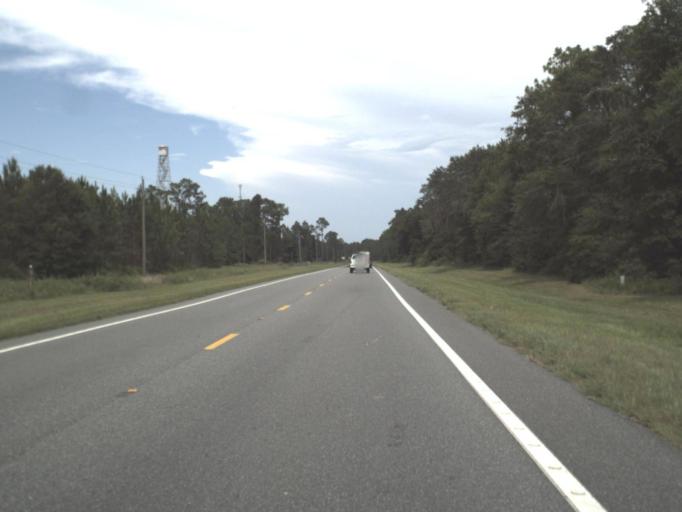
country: US
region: Florida
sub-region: Taylor County
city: Perry
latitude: 30.1001
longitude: -83.4559
